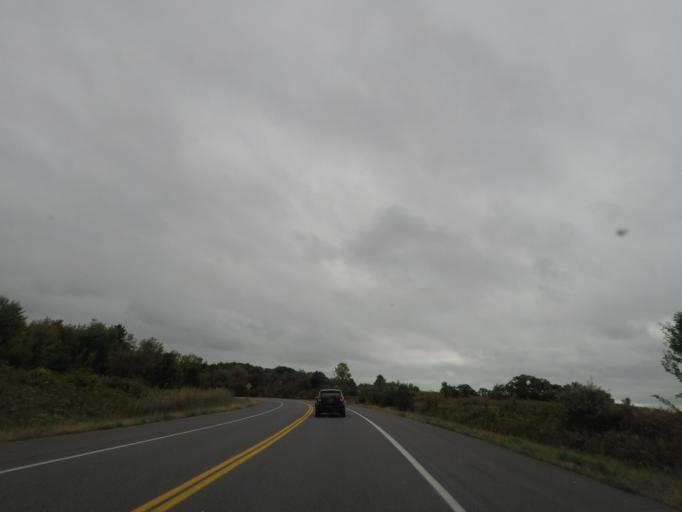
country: US
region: New York
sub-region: Rensselaer County
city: Hampton Manor
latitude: 42.6525
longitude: -73.6917
